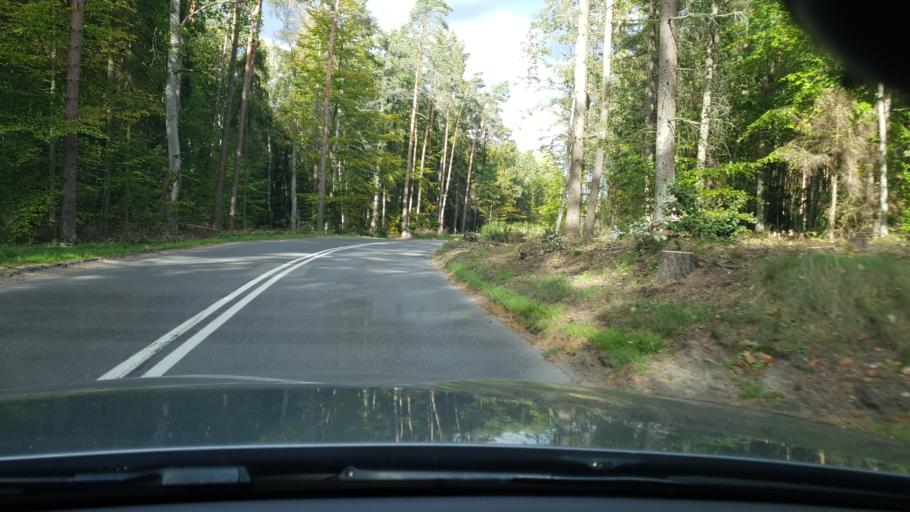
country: PL
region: Pomeranian Voivodeship
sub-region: Powiat wejherowski
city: Koleczkowo
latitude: 54.5005
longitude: 18.3640
